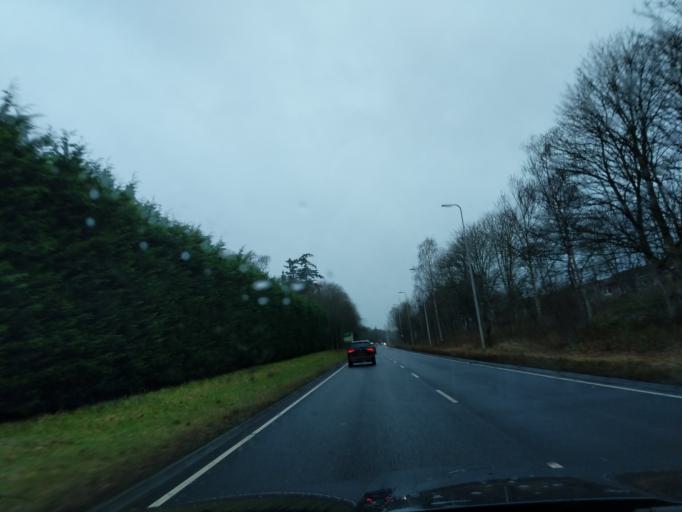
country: GB
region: Scotland
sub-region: The Scottish Borders
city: Melrose
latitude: 55.5967
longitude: -2.7318
